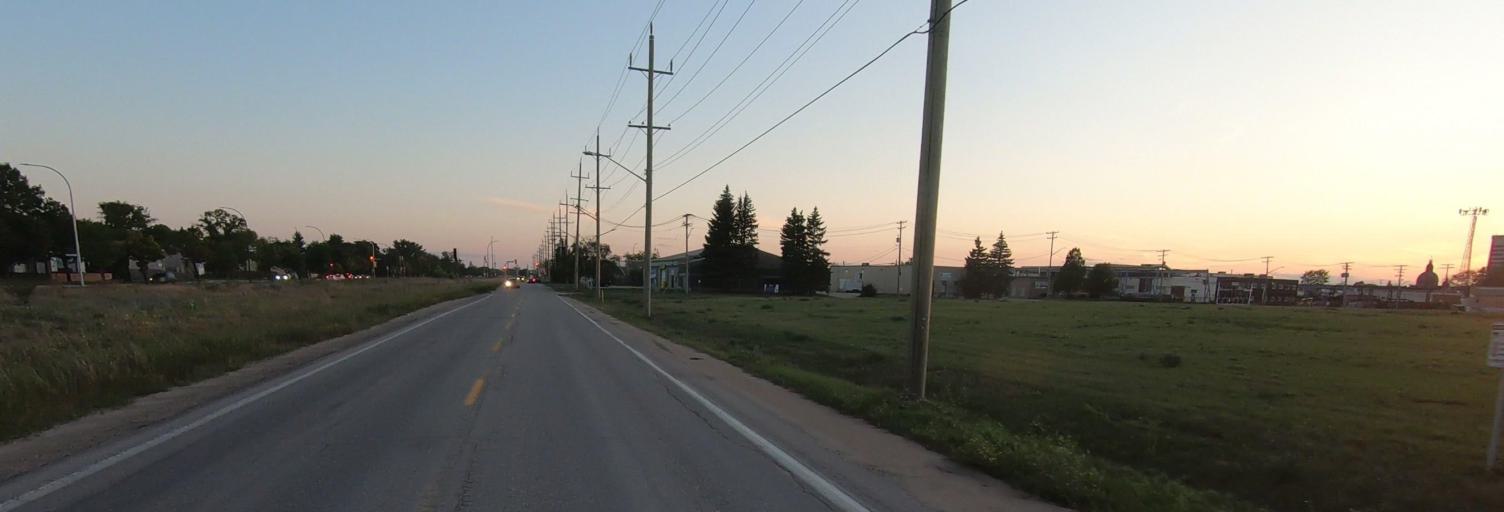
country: CA
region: Manitoba
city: Winnipeg
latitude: 49.9170
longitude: -97.0872
